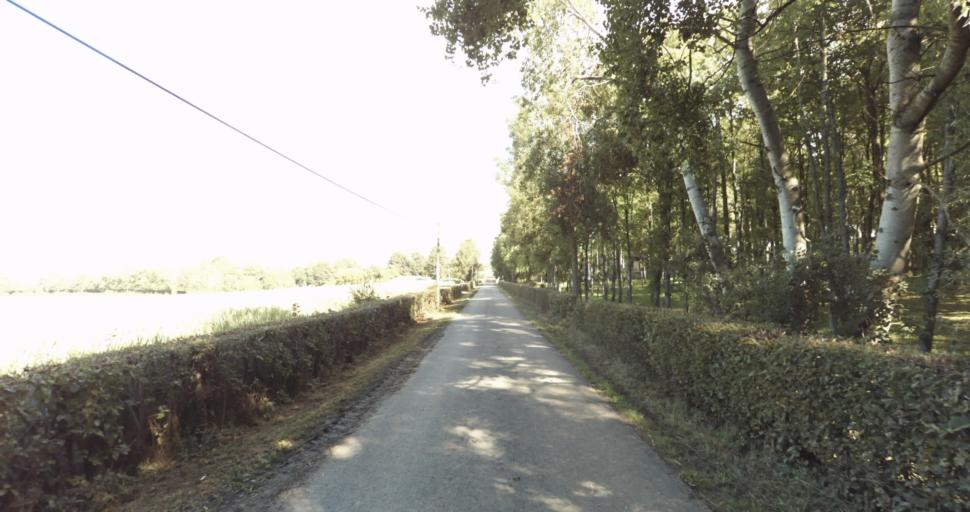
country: FR
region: Lower Normandy
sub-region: Departement de l'Orne
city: Gace
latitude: 48.8113
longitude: 0.2258
